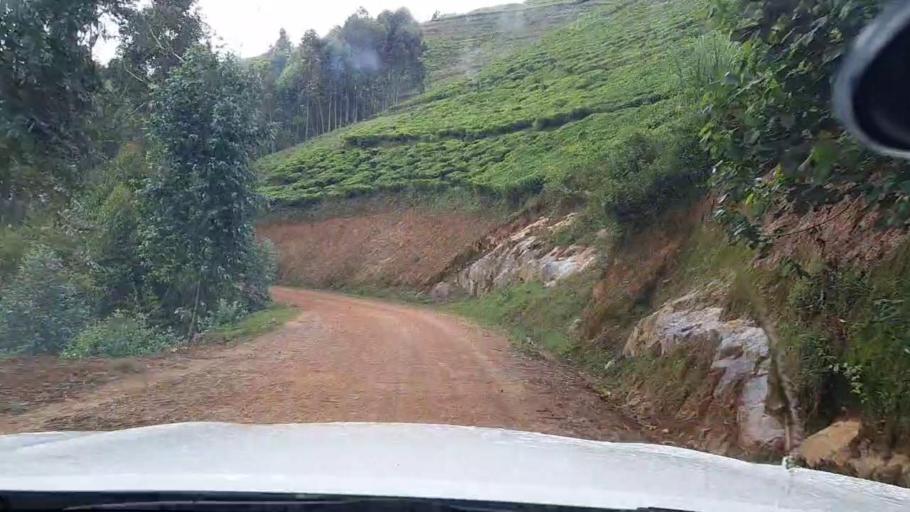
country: RW
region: Western Province
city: Kibuye
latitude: -2.1584
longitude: 29.4347
